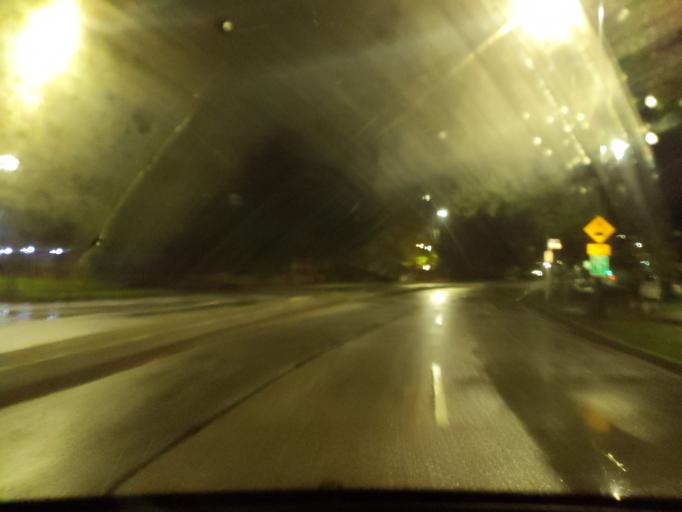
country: CA
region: British Columbia
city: New Westminster
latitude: 49.1918
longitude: -122.8507
